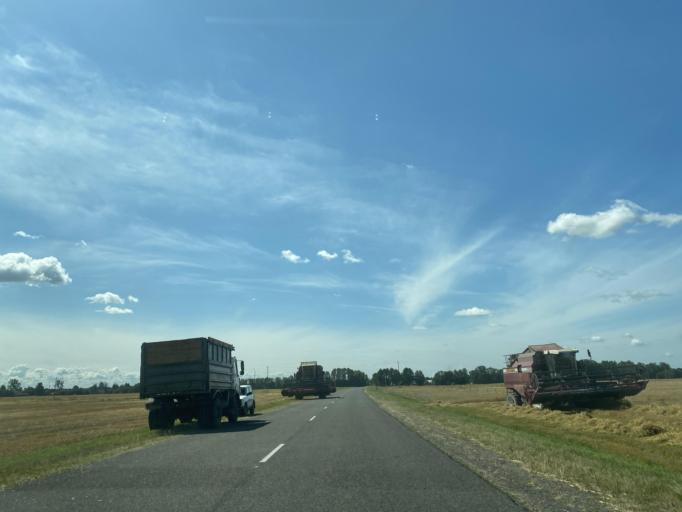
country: BY
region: Brest
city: Ivanava
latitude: 52.1962
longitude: 25.6128
